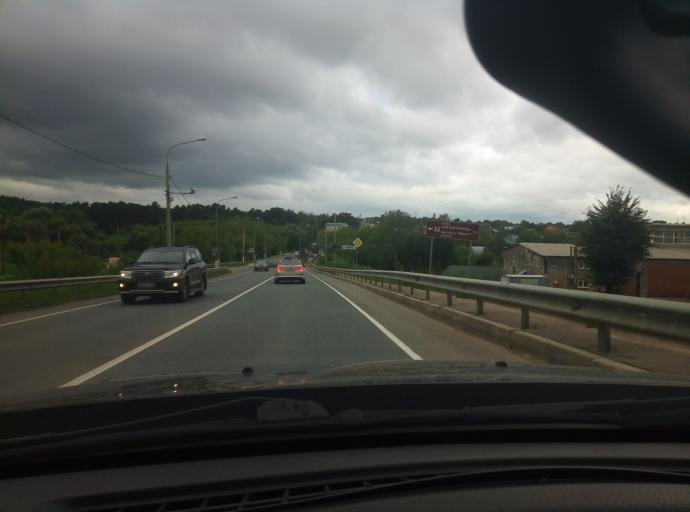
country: RU
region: Moskovskaya
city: Danki
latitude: 54.9114
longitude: 37.4935
